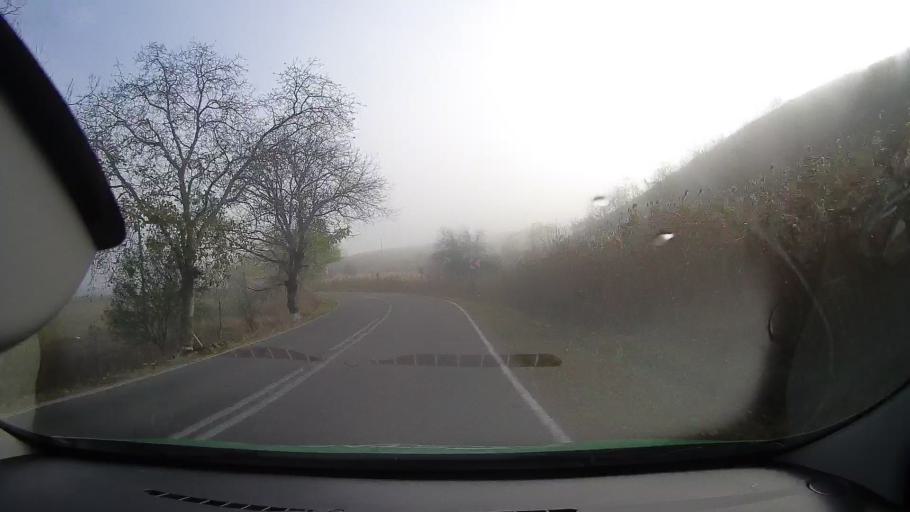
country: RO
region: Tulcea
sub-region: Comuna Nufaru
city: Malcoci
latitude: 45.1461
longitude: 28.9013
